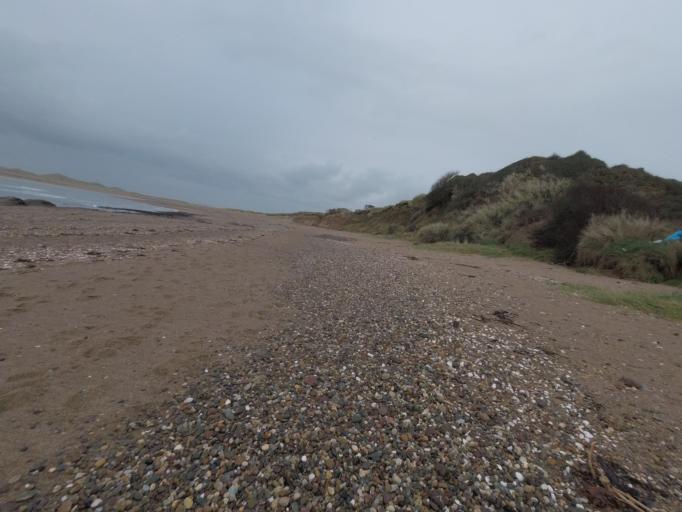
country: IE
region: Munster
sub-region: Waterford
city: Tra Mhor
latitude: 52.1434
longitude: -7.0915
